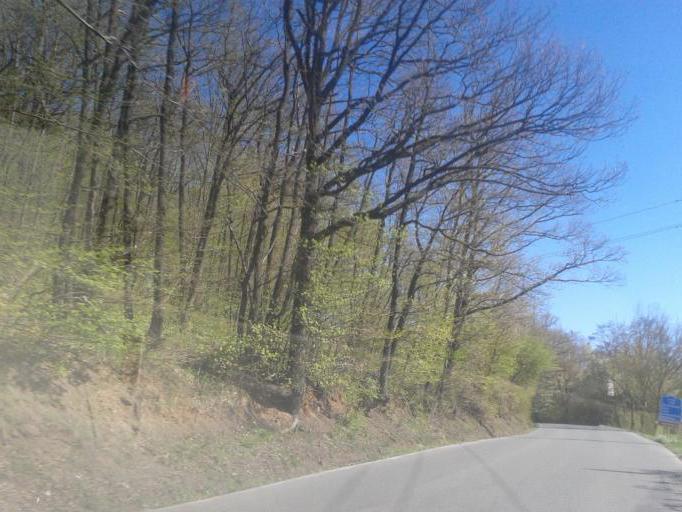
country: CZ
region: Central Bohemia
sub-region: Okres Beroun
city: Beroun
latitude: 49.9196
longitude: 14.0730
